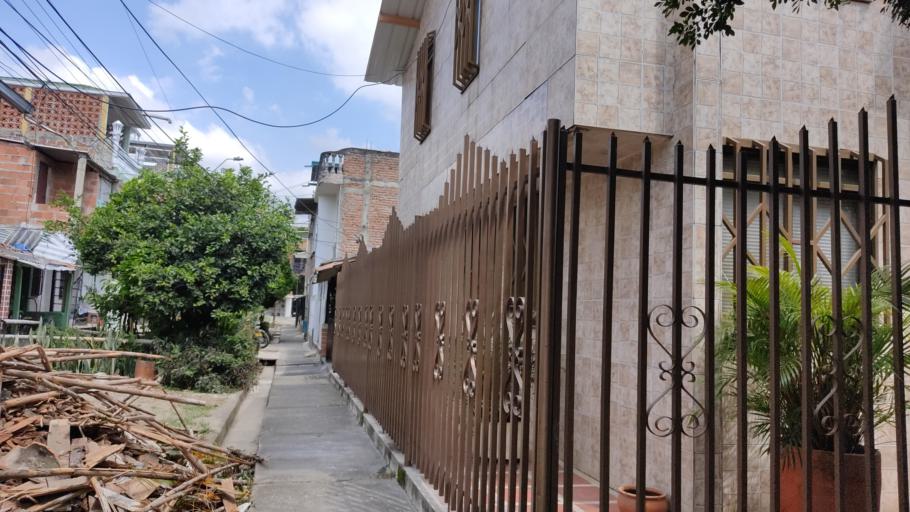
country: CO
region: Valle del Cauca
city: Jamundi
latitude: 3.2515
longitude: -76.5418
